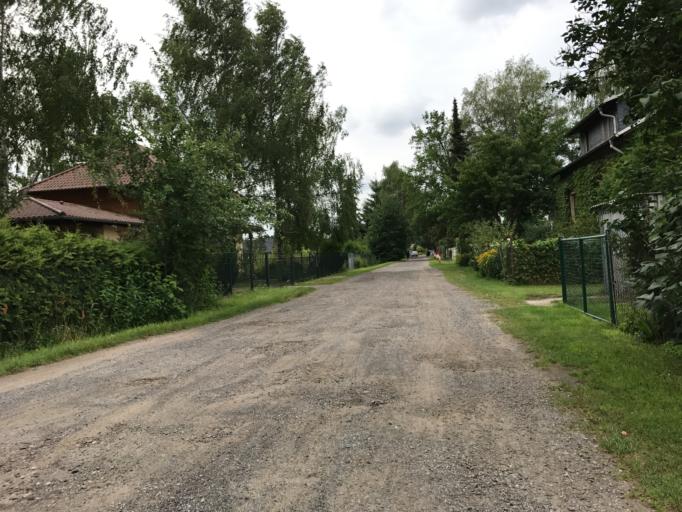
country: DE
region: Berlin
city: Karow
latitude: 52.6154
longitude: 13.4814
